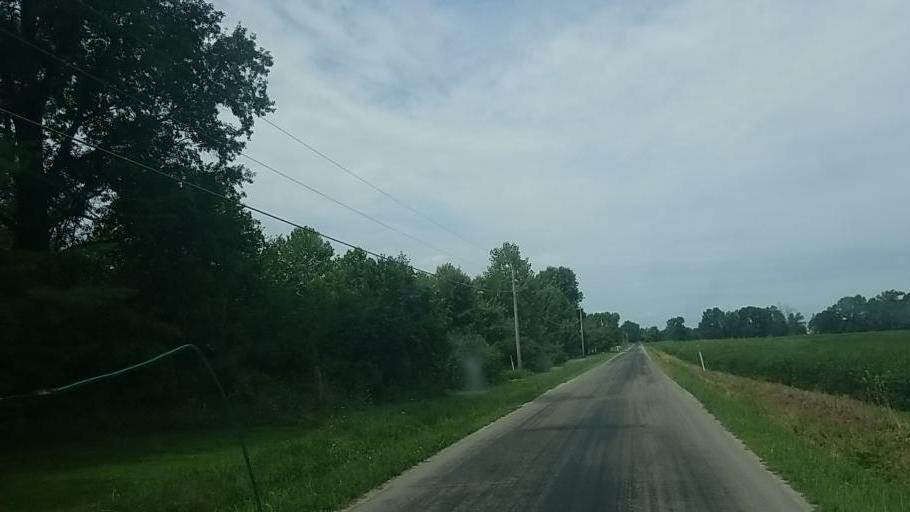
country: US
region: Ohio
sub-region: Delaware County
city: Sunbury
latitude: 40.2023
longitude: -82.7877
